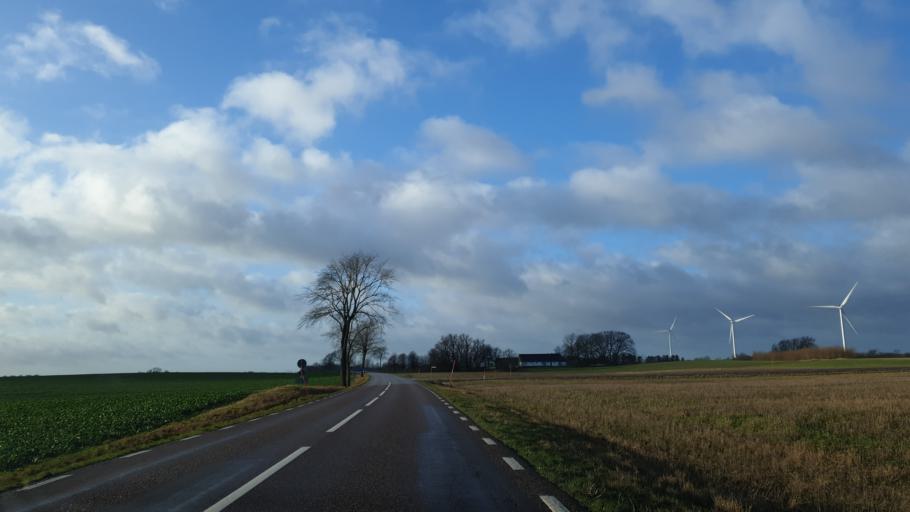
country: SE
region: Skane
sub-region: Trelleborgs Kommun
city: Anderslov
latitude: 55.4246
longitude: 13.4259
